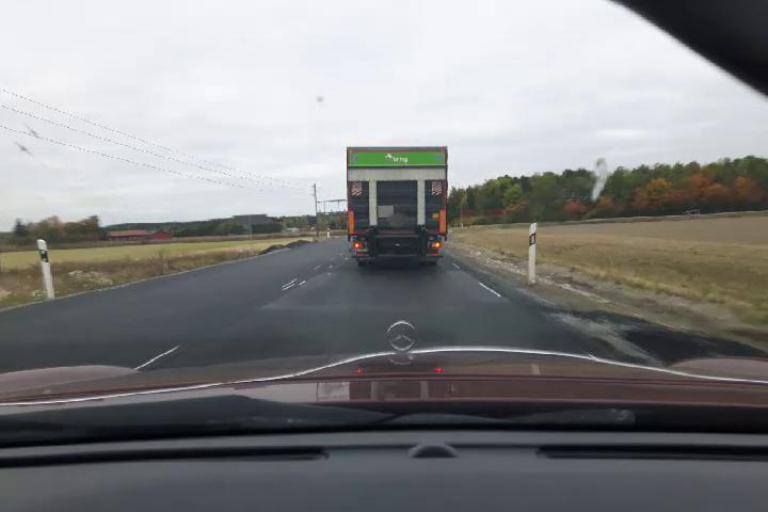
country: SE
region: Uppsala
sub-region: Enkopings Kommun
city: Enkoping
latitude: 59.6310
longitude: 17.0488
